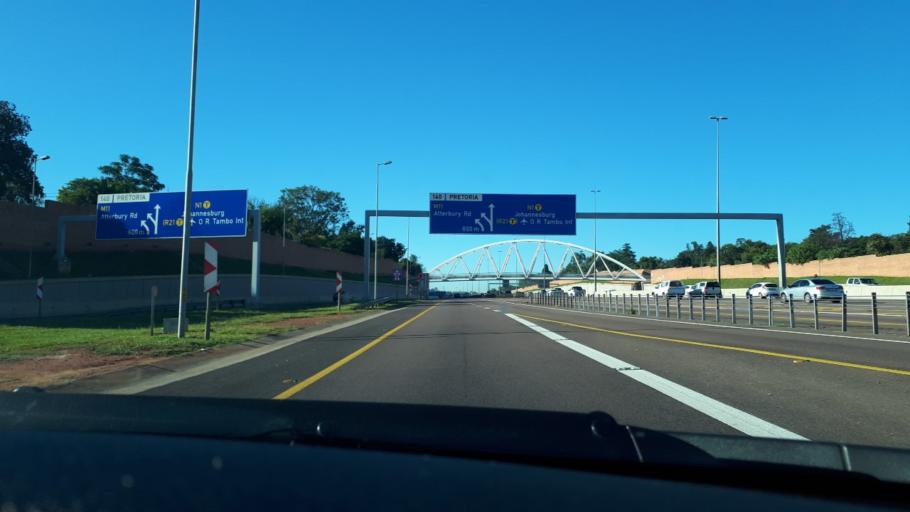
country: ZA
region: Gauteng
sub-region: City of Tshwane Metropolitan Municipality
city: Pretoria
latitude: -25.7671
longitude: 28.2751
